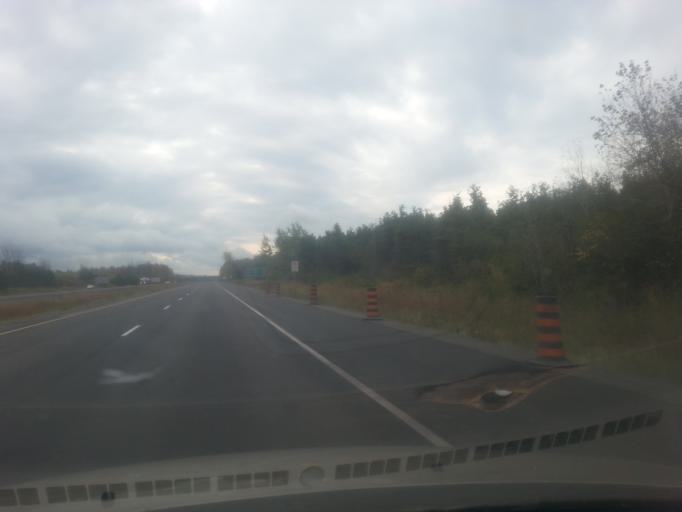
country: CA
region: Ontario
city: Bells Corners
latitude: 45.2019
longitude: -75.7308
